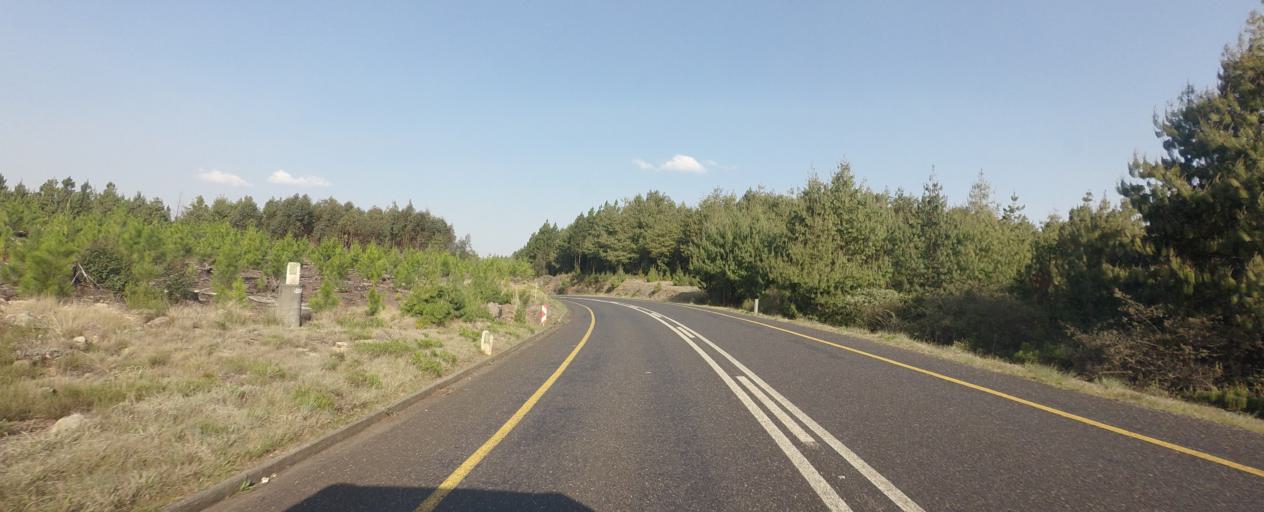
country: ZA
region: Mpumalanga
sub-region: Ehlanzeni District
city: Lydenburg
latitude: -25.1773
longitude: 30.6527
